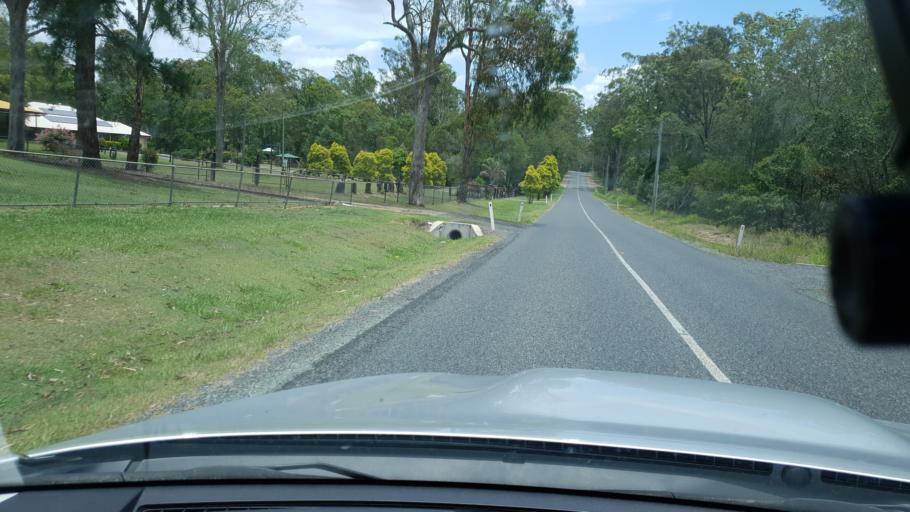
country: AU
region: Queensland
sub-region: Logan
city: North Maclean
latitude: -27.7714
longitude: 152.9863
